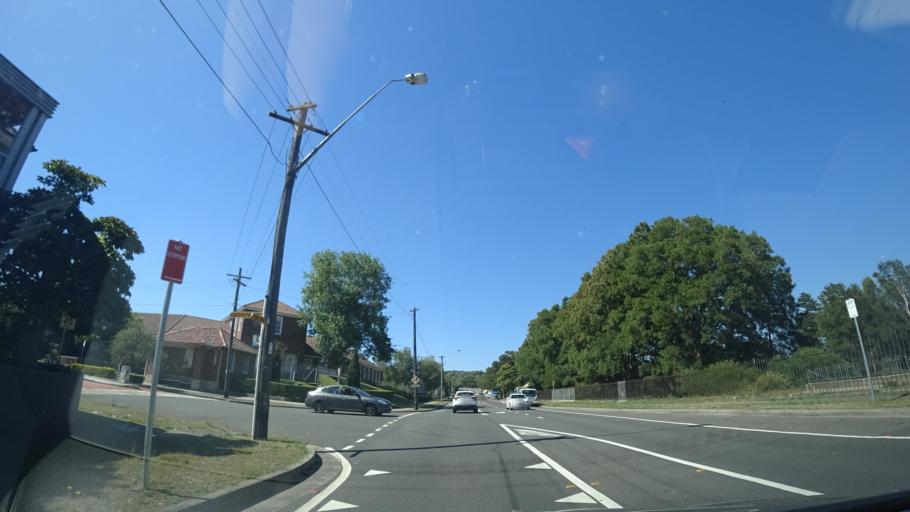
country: AU
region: New South Wales
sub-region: Waverley
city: Bondi Junction
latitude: -33.8980
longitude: 151.2424
